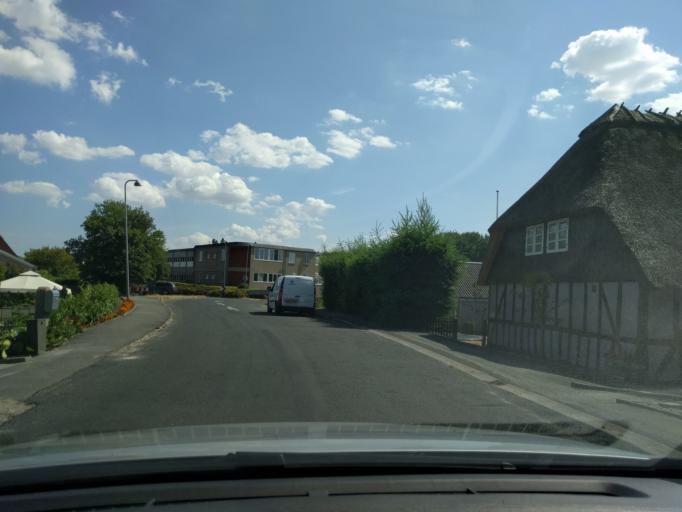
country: DK
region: South Denmark
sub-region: Odense Kommune
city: Odense
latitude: 55.4188
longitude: 10.3712
